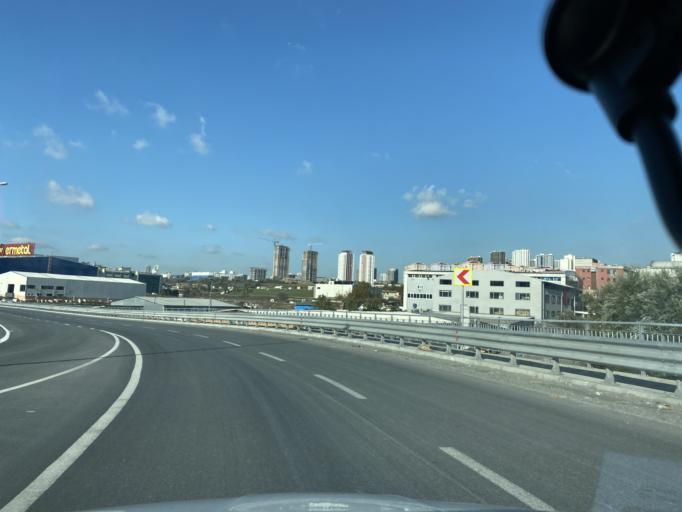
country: TR
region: Istanbul
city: Esenyurt
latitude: 41.0592
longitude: 28.6516
